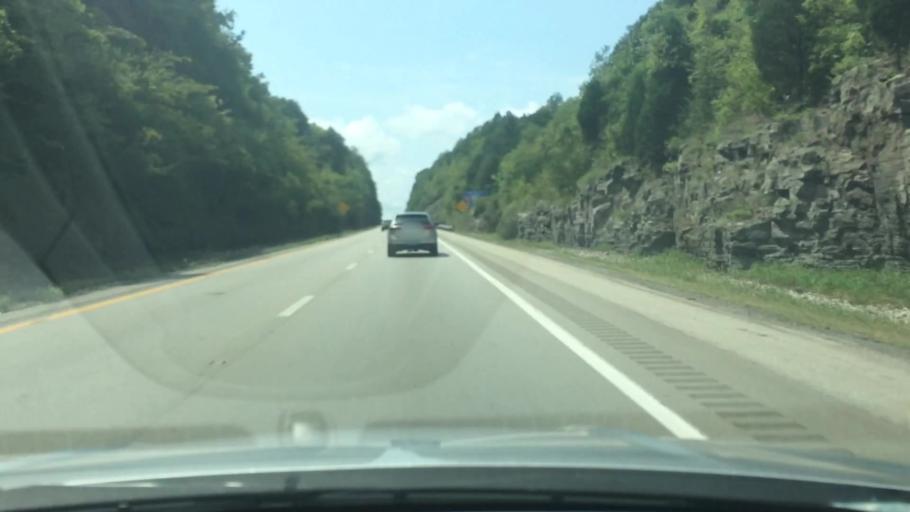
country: US
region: Kentucky
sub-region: Franklin County
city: Frankfort
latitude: 38.1600
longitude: -84.8652
